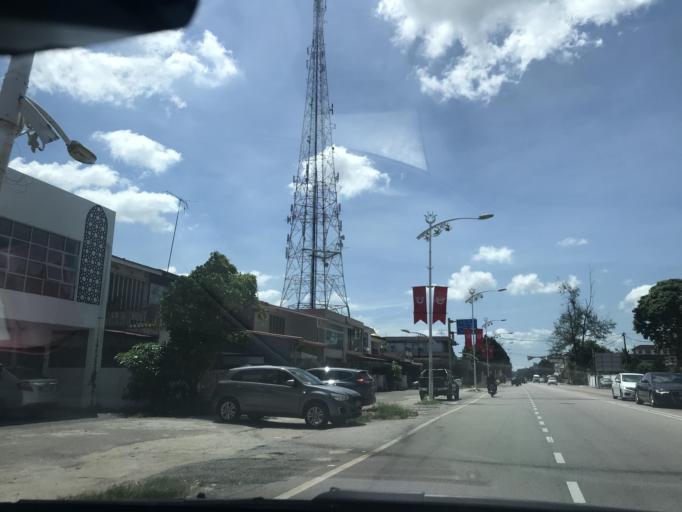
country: MY
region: Kelantan
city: Kota Bharu
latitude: 6.1091
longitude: 102.2420
